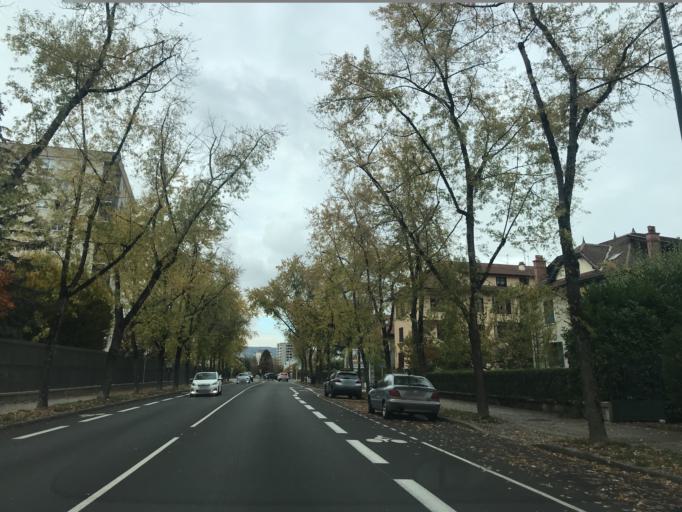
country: FR
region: Rhone-Alpes
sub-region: Departement de la Haute-Savoie
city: Annecy-le-Vieux
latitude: 45.9135
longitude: 6.1305
